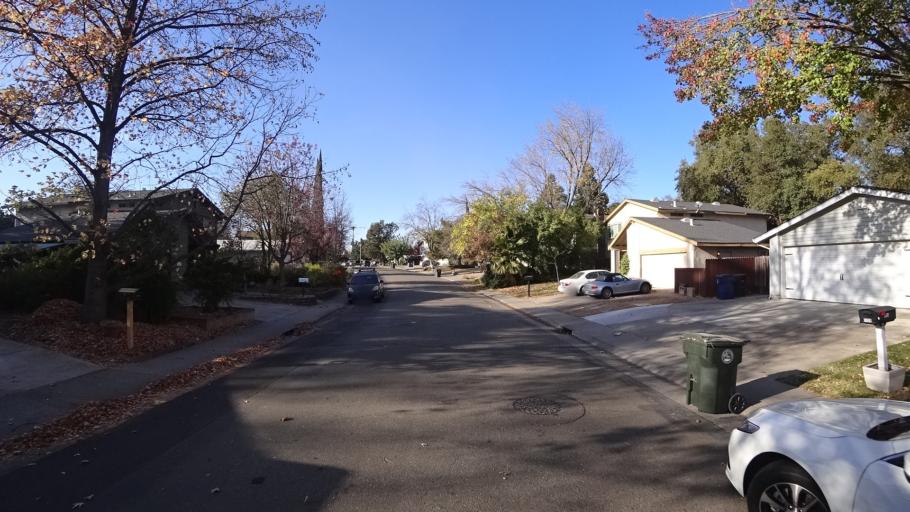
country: US
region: California
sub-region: Sacramento County
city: Antelope
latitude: 38.6967
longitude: -121.3146
